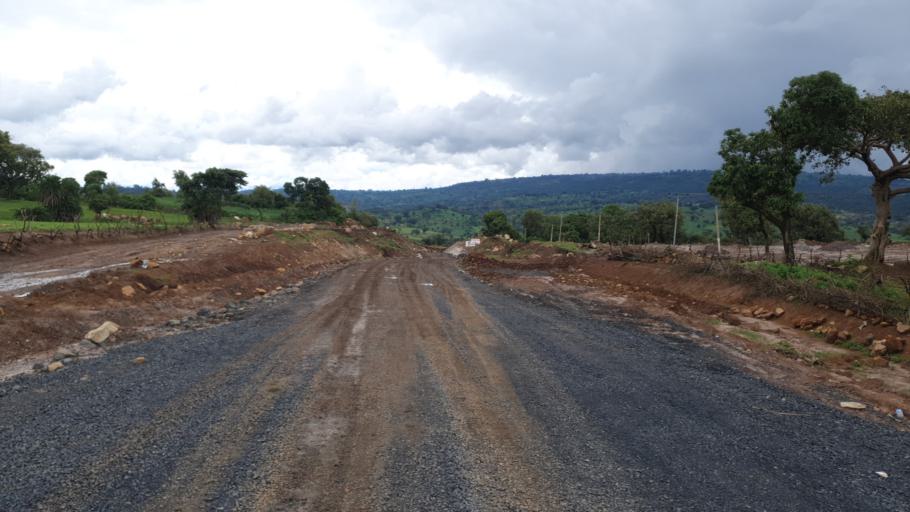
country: ET
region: Oromiya
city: Shambu
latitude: 10.0822
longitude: 36.8833
